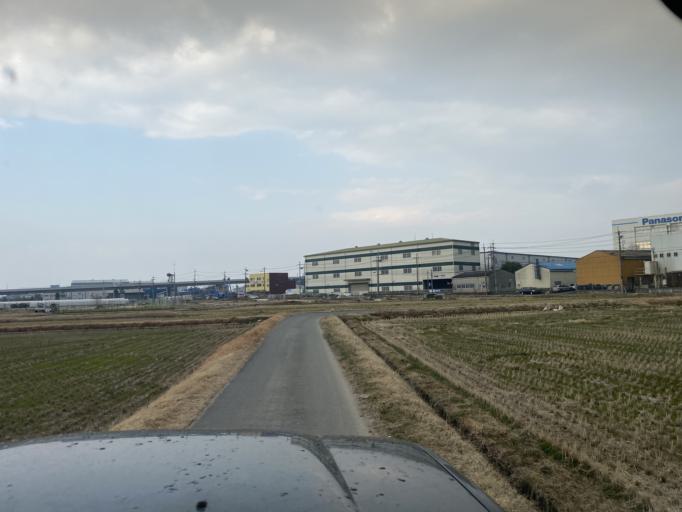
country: JP
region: Kyoto
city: Tanabe
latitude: 34.8424
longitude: 135.7484
